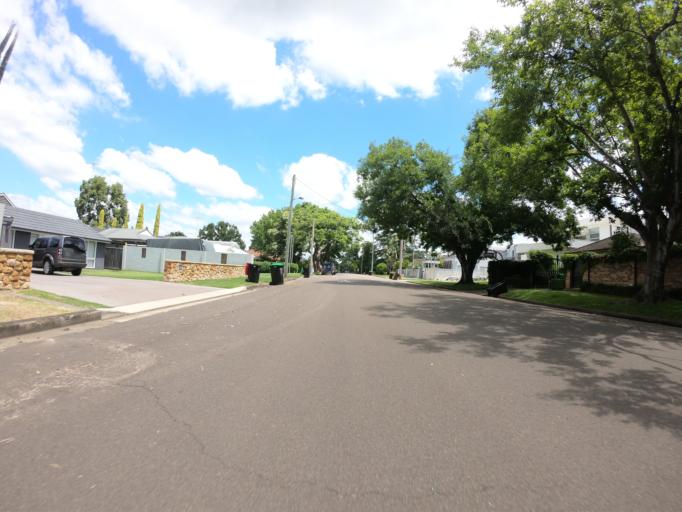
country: AU
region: New South Wales
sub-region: Penrith Municipality
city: Penrith
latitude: -33.7496
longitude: 150.6808
